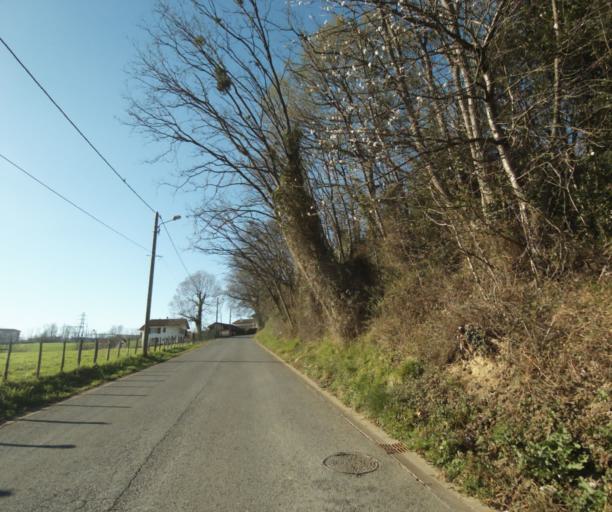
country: FR
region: Aquitaine
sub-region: Departement des Pyrenees-Atlantiques
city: Hendaye
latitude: 43.3605
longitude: -1.7547
